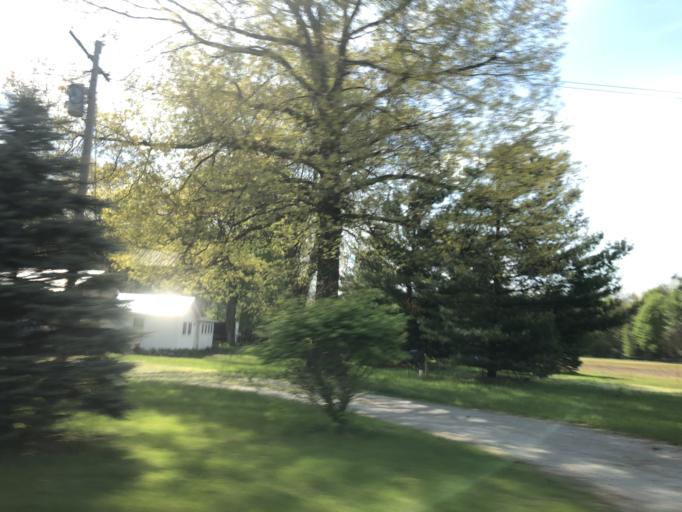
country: US
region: Michigan
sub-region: Hillsdale County
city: Reading
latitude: 41.7498
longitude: -84.8147
